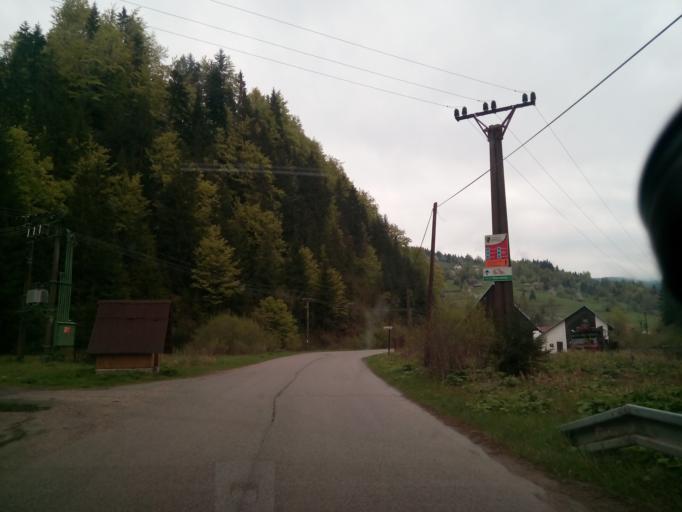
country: SK
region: Zilinsky
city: Oravska Lesna
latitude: 49.2957
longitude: 19.1803
